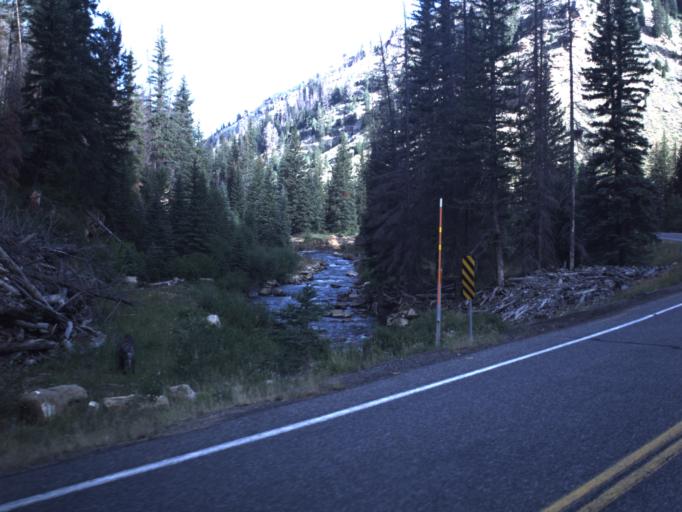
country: US
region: Utah
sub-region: Emery County
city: Huntington
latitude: 39.4987
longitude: -111.1574
